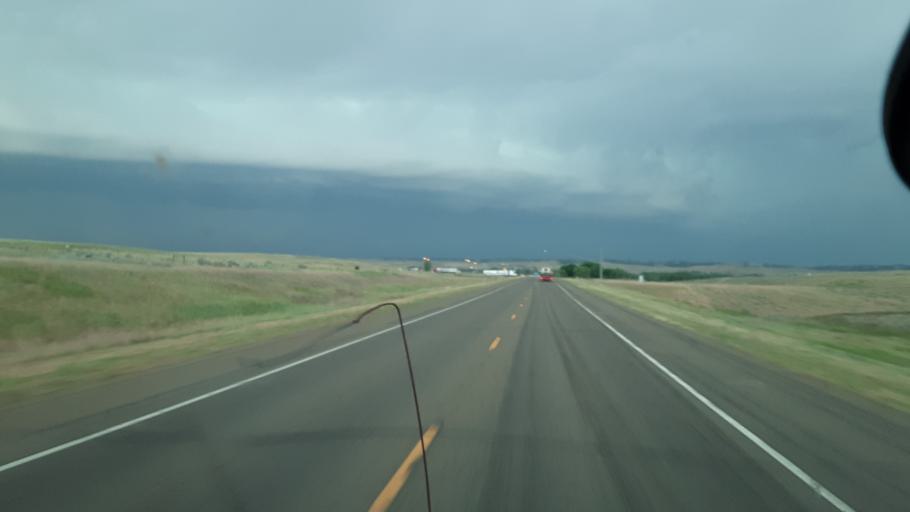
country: US
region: Montana
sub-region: Powder River County
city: Broadus
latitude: 45.4176
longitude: -105.3904
